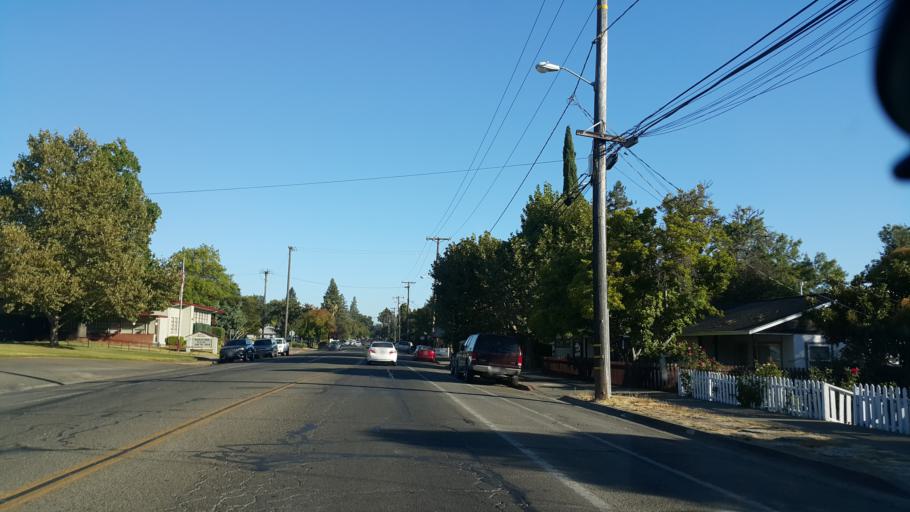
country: US
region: California
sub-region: Mendocino County
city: Ukiah
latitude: 39.1413
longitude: -123.2104
